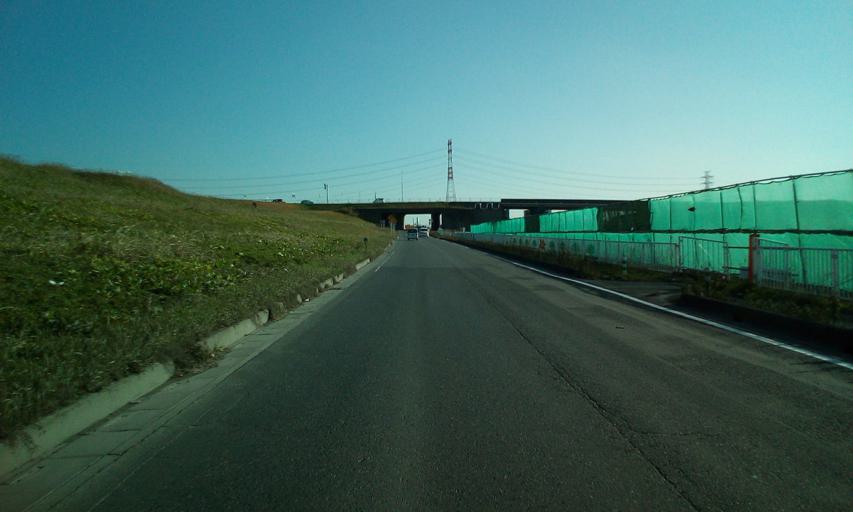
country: JP
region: Chiba
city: Noda
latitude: 35.9139
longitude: 139.8686
